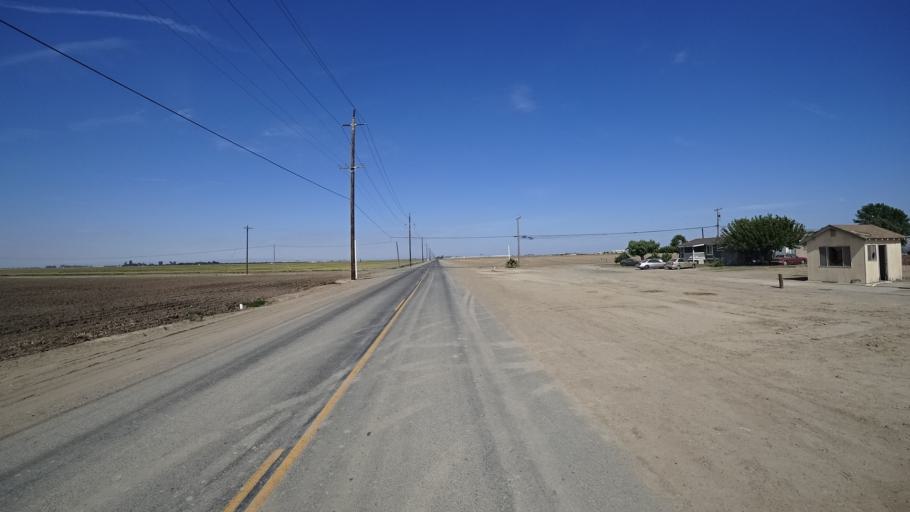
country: US
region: California
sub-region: Kings County
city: Home Garden
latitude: 36.2549
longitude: -119.6181
